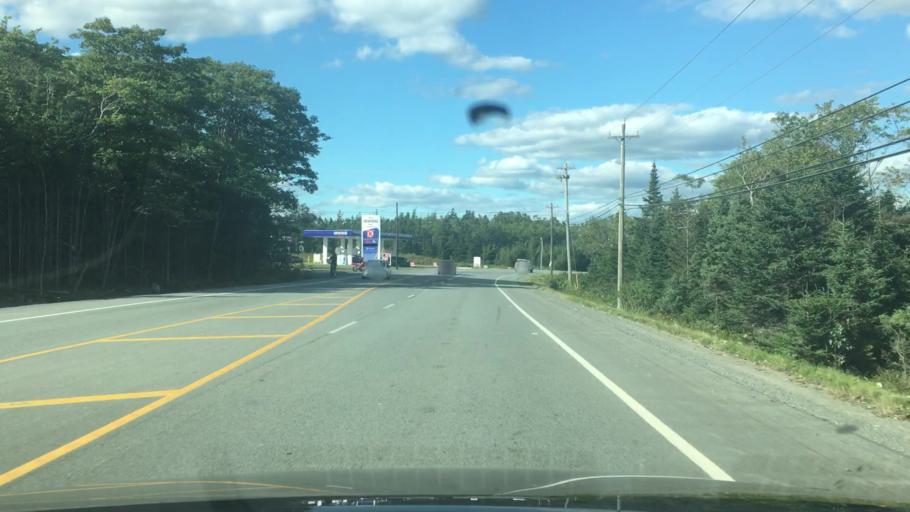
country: CA
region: Nova Scotia
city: Halifax
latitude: 44.6066
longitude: -63.6727
